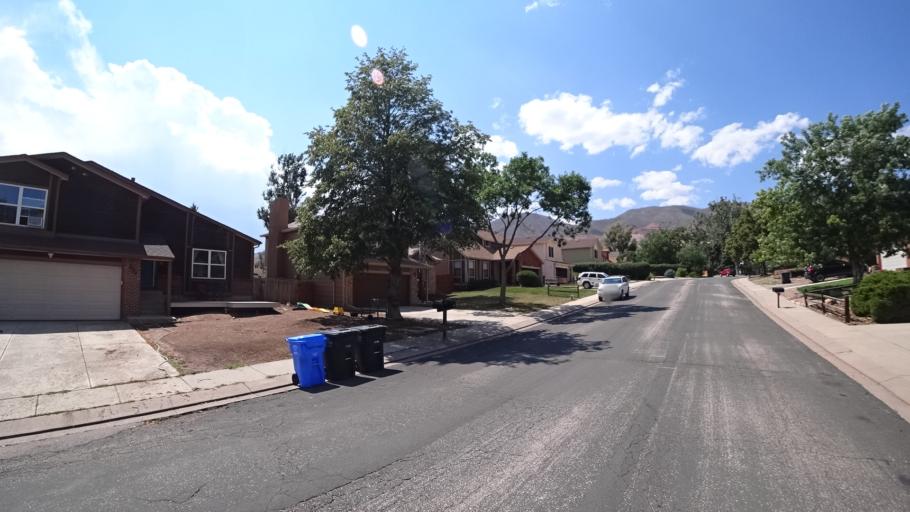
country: US
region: Colorado
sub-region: El Paso County
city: Air Force Academy
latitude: 38.9336
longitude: -104.8708
